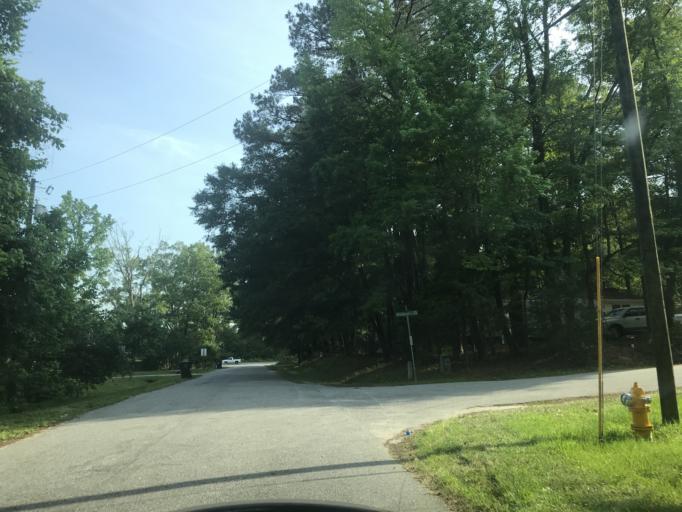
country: US
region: North Carolina
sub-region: Wake County
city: Garner
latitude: 35.7423
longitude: -78.5712
